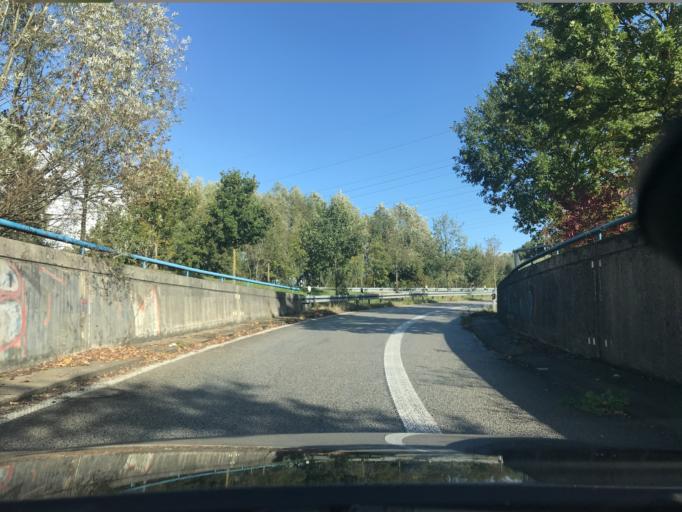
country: DE
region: North Rhine-Westphalia
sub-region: Regierungsbezirk Dusseldorf
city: Meerbusch
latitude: 51.2948
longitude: 6.6565
